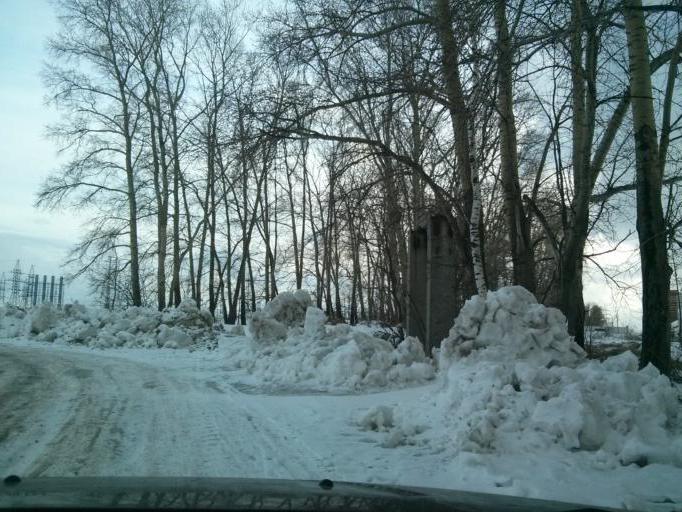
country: RU
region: Nizjnij Novgorod
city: Afonino
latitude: 56.2689
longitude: 44.0315
